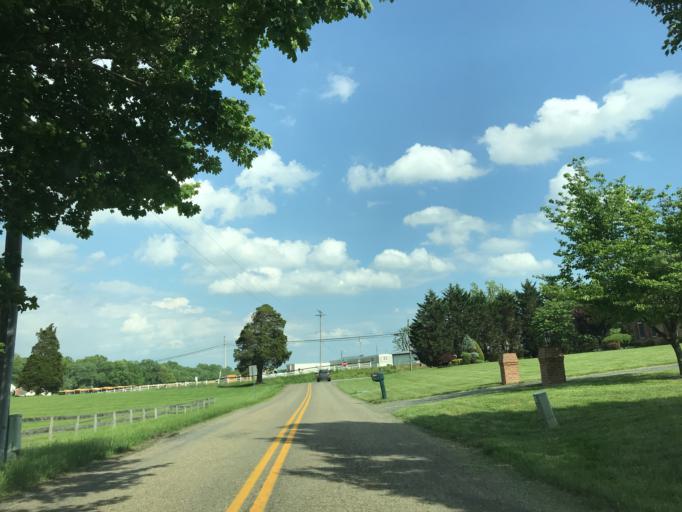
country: US
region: Maryland
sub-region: Harford County
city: Bel Air North
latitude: 39.6106
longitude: -76.3672
